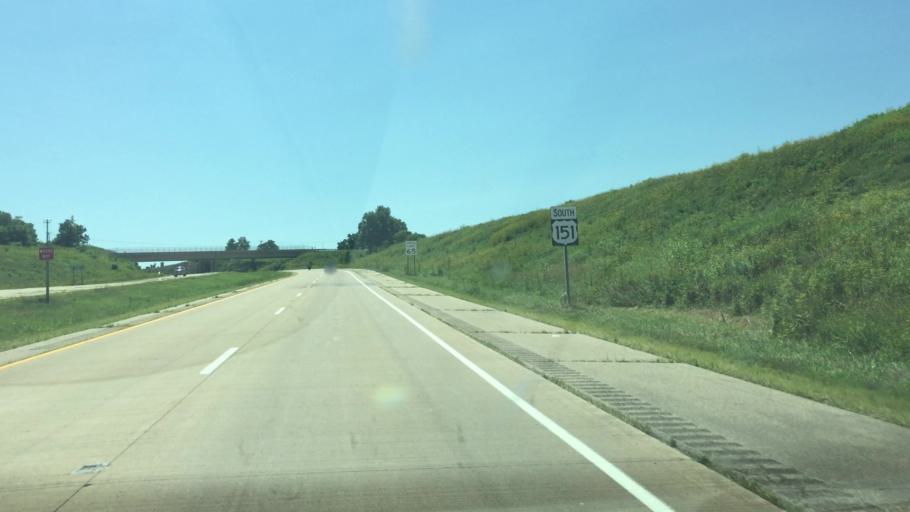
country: US
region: Wisconsin
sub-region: Iowa County
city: Mineral Point
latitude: 42.8239
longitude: -90.2466
